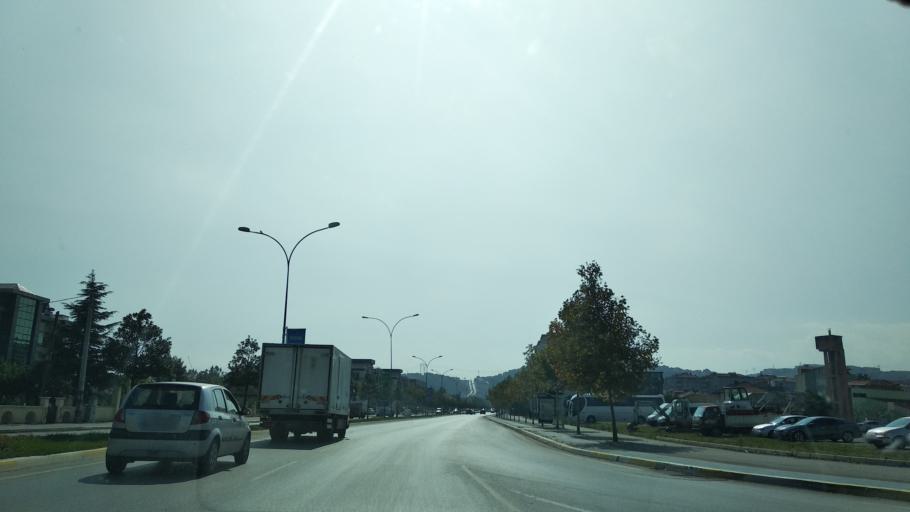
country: TR
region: Sakarya
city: Adapazari
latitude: 40.7719
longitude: 30.3641
